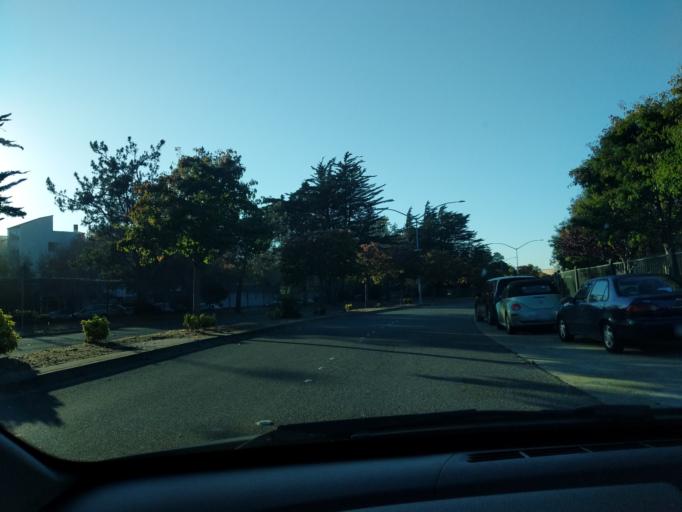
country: US
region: California
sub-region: Contra Costa County
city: Richmond
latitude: 37.9161
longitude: -122.3482
